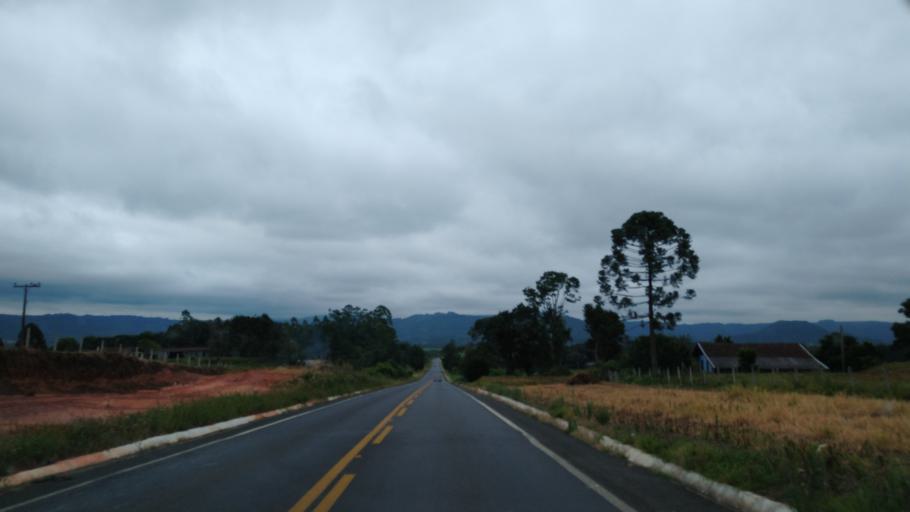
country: BR
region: Santa Catarina
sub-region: Porto Uniao
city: Porto Uniao
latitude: -26.2829
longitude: -51.0064
